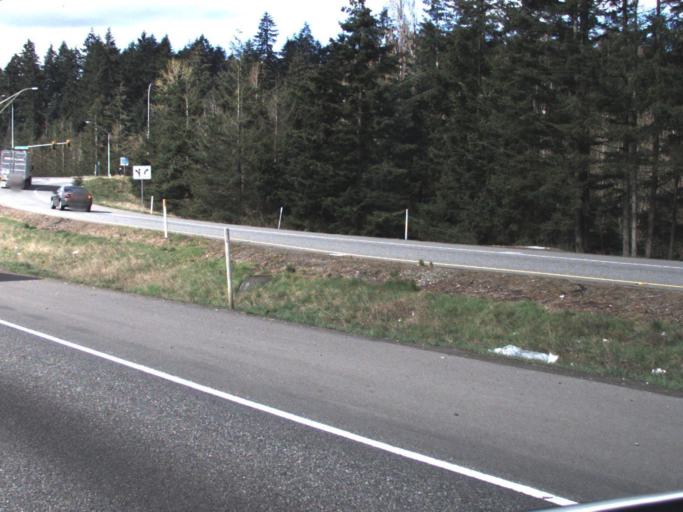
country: US
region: Washington
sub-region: King County
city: Lakeland South
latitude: 47.2954
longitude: -122.2899
